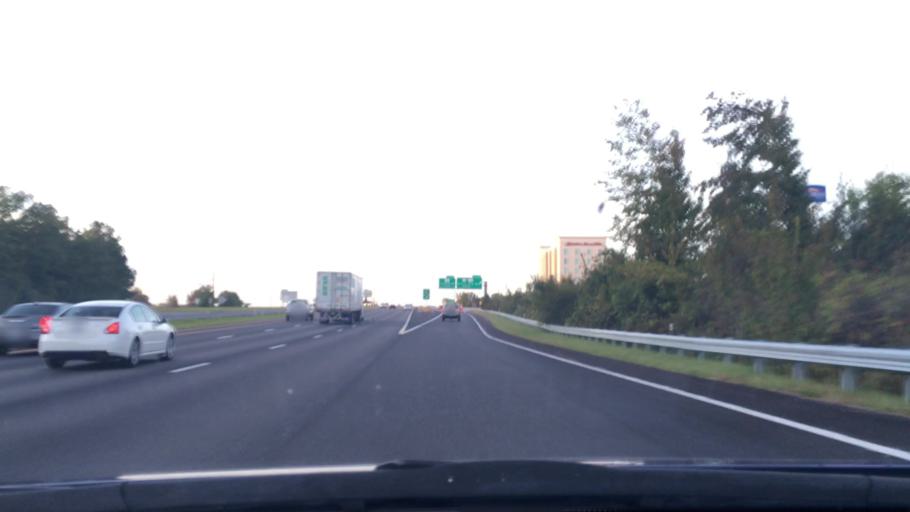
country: US
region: South Carolina
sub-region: Richland County
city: Forest Acres
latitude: 33.9673
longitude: -80.9532
